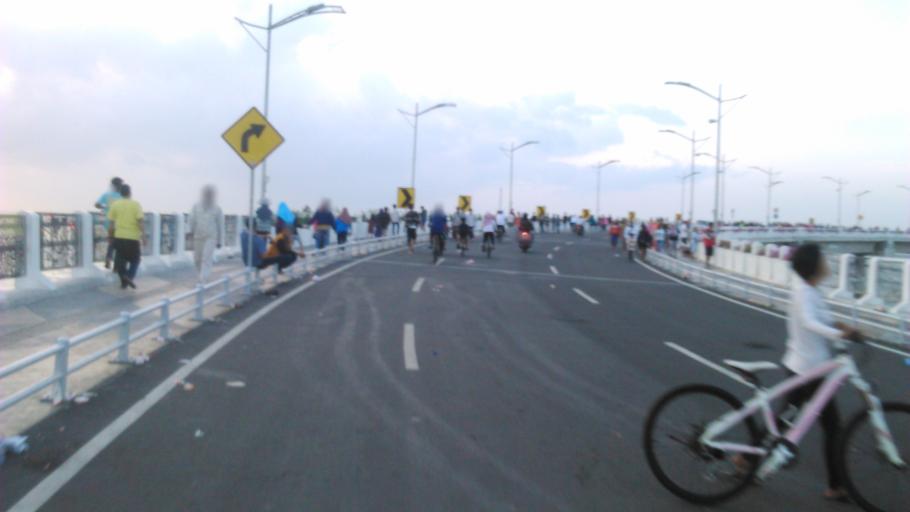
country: ID
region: East Java
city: Labansari
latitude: -7.2359
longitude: 112.7965
